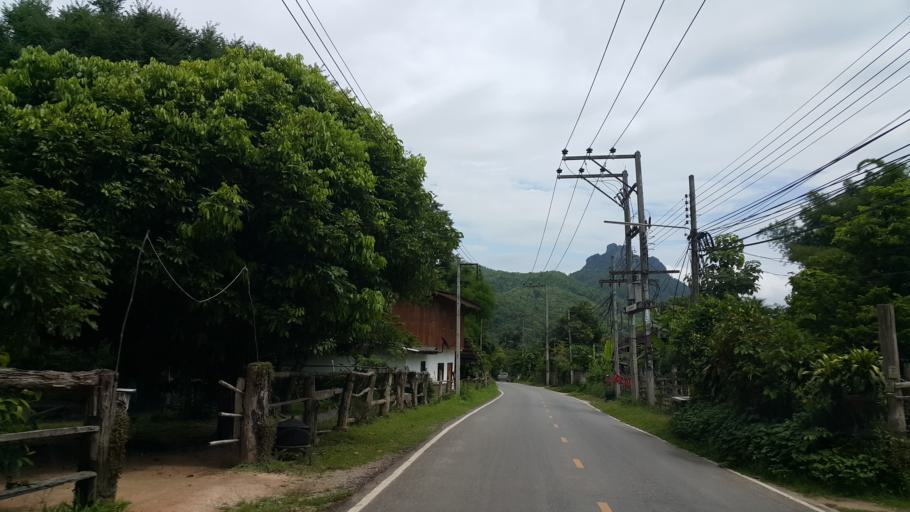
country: TH
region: Lampang
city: Mueang Pan
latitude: 18.7775
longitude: 99.5249
